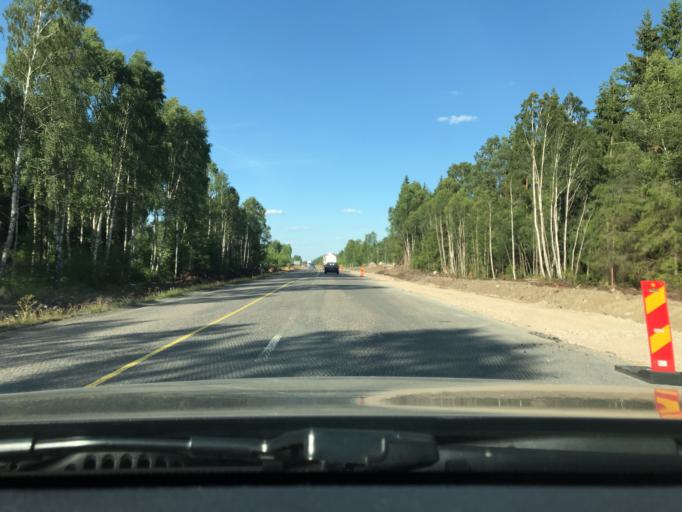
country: SE
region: Kronoberg
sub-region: Almhults Kommun
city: AElmhult
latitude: 56.5536
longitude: 14.1718
